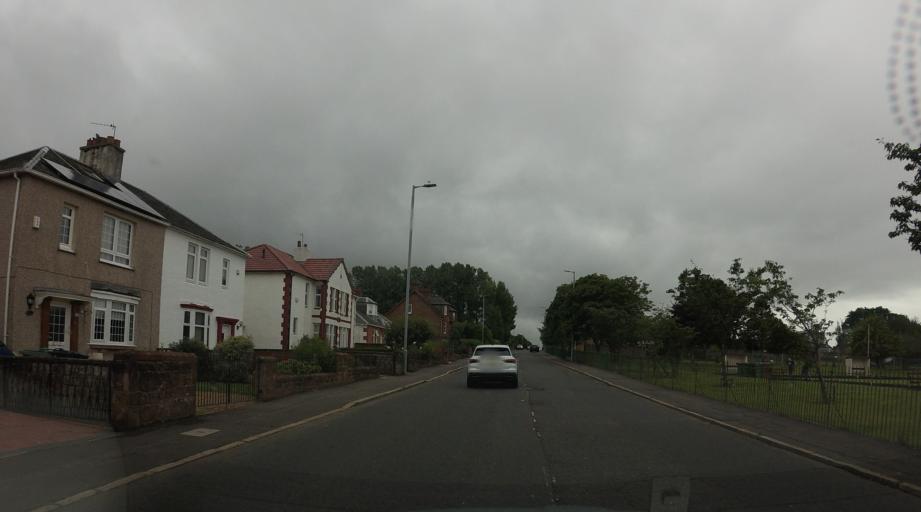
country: GB
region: Scotland
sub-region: South Ayrshire
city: Ayr
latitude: 55.4649
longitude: -4.6183
